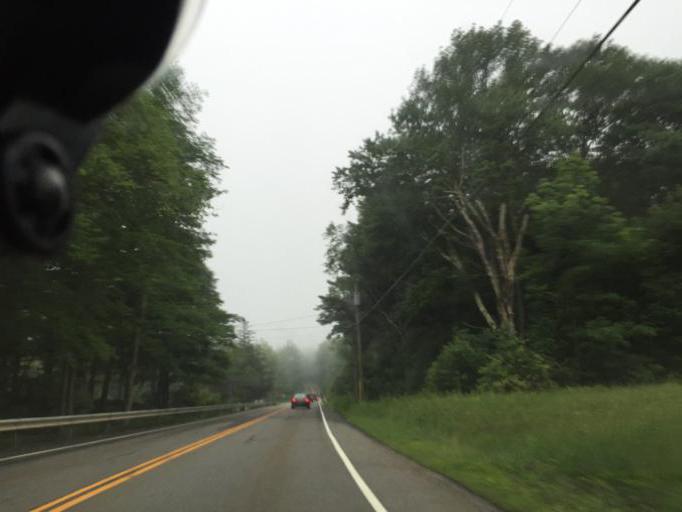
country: US
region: Connecticut
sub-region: Litchfield County
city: Winchester Center
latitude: 41.8901
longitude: -73.2555
